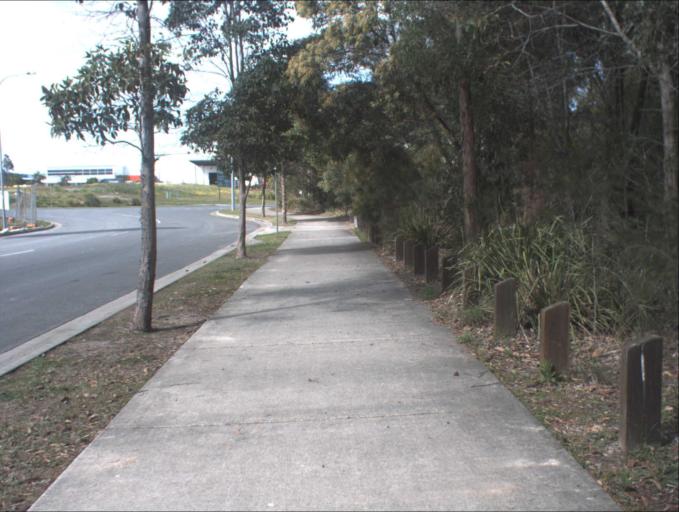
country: AU
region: Queensland
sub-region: Logan
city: Woodridge
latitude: -27.6689
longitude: 153.0759
